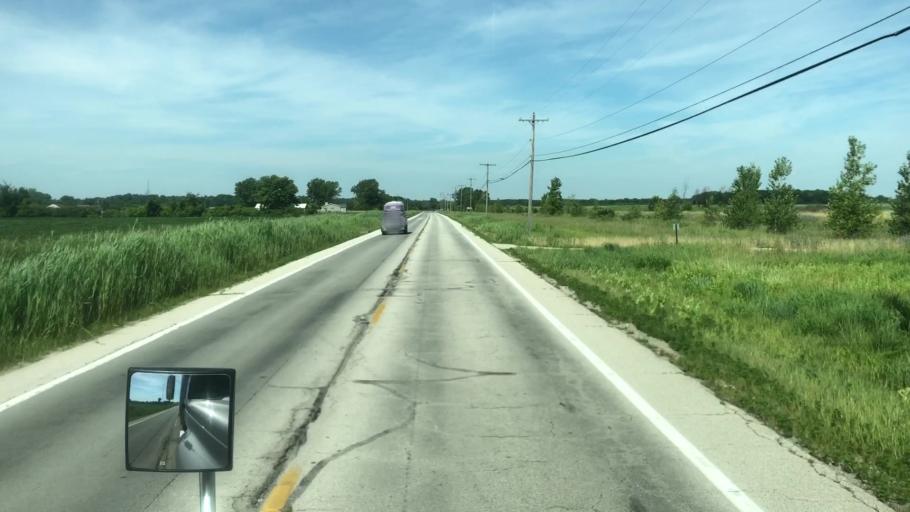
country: US
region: Ohio
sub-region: Ottawa County
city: Port Clinton
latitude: 41.4085
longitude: -82.9267
